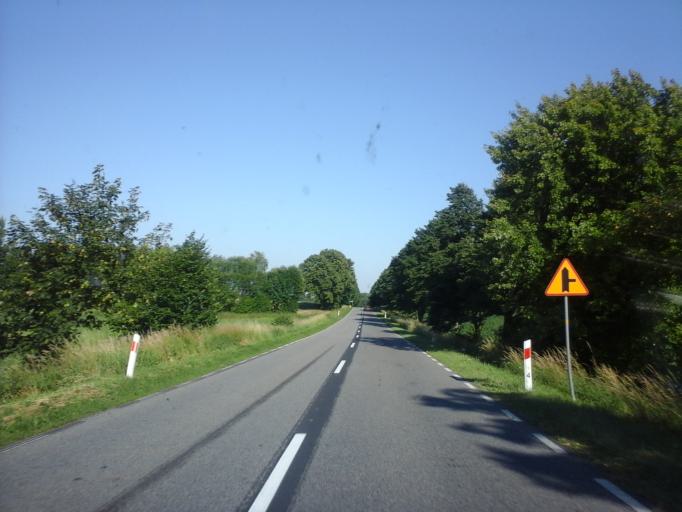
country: PL
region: West Pomeranian Voivodeship
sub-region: Powiat goleniowski
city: Nowogard
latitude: 53.6523
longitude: 15.2031
